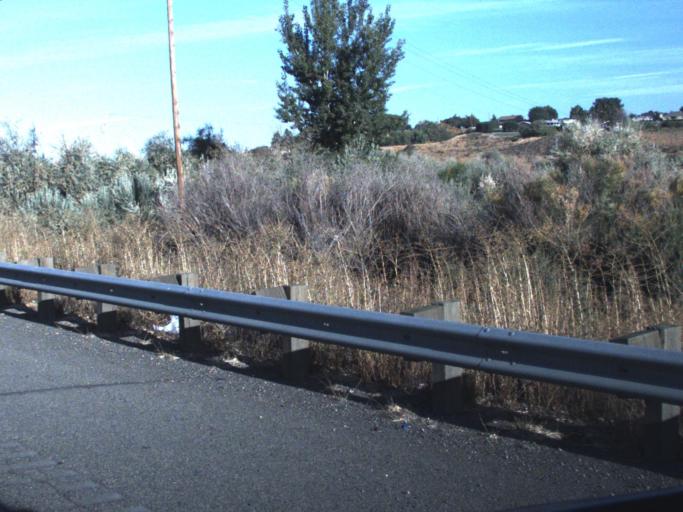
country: US
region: Washington
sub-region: Yakima County
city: Sunnyside
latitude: 46.3068
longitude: -120.0409
